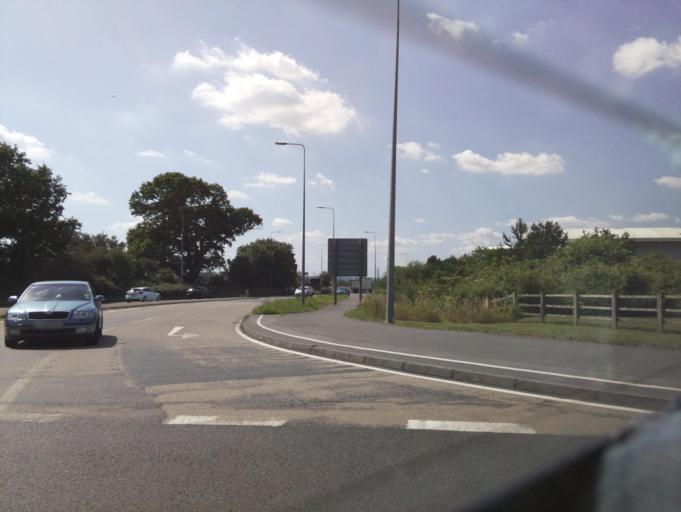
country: GB
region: England
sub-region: Leicestershire
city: Hinckley
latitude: 52.5253
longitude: -1.3876
